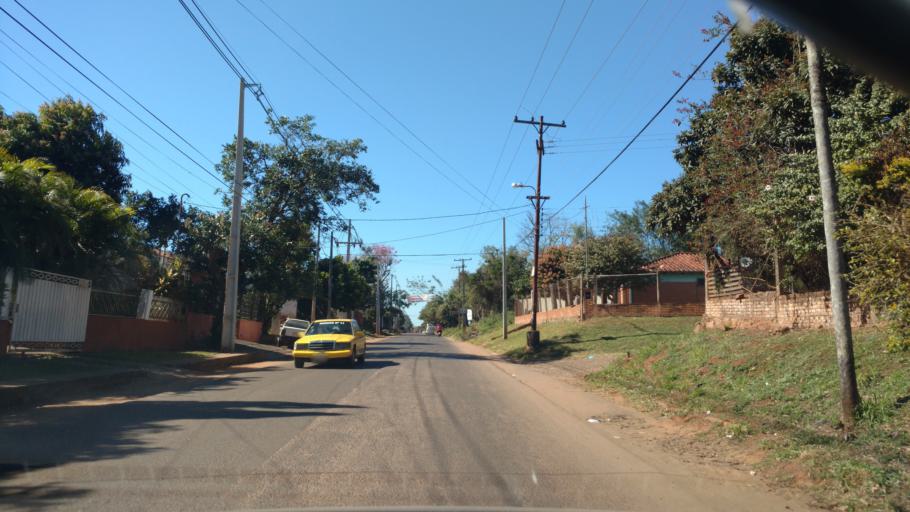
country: PY
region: Central
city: Itaugua
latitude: -25.4000
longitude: -57.3422
